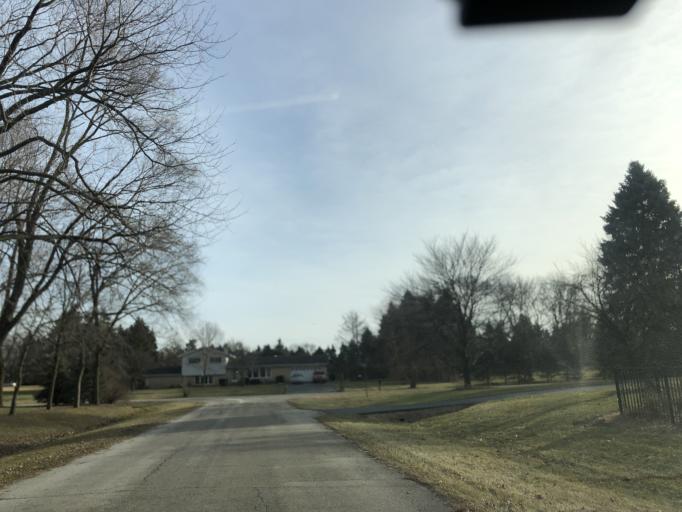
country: US
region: Illinois
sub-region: Cook County
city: Lemont
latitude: 41.7120
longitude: -88.0133
